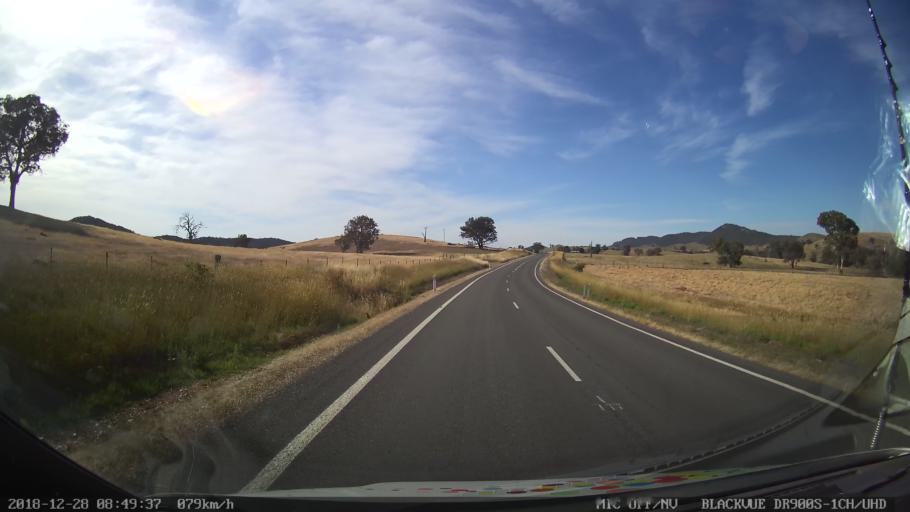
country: AU
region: New South Wales
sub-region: Upper Lachlan Shire
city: Crookwell
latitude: -34.0475
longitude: 149.3376
